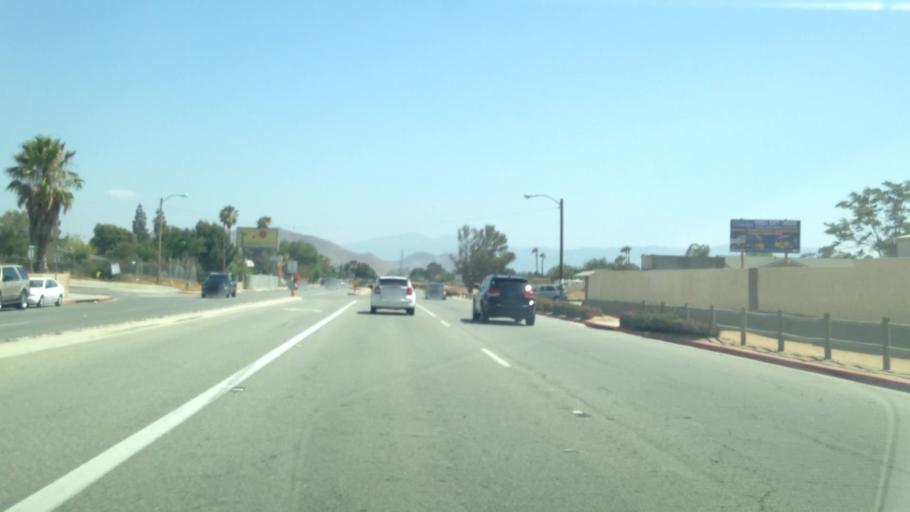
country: US
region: California
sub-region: Riverside County
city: Mira Loma
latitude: 33.9907
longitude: -117.5234
